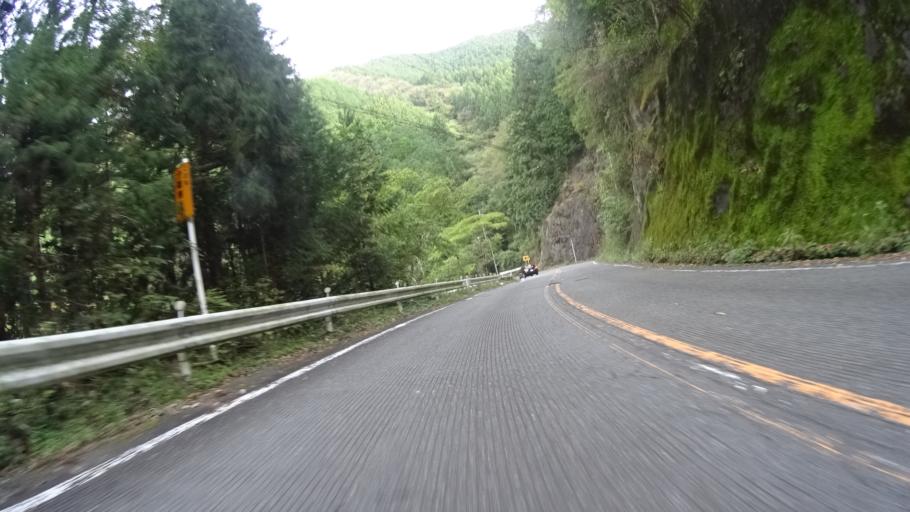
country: JP
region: Yamanashi
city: Uenohara
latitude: 35.6864
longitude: 139.1010
